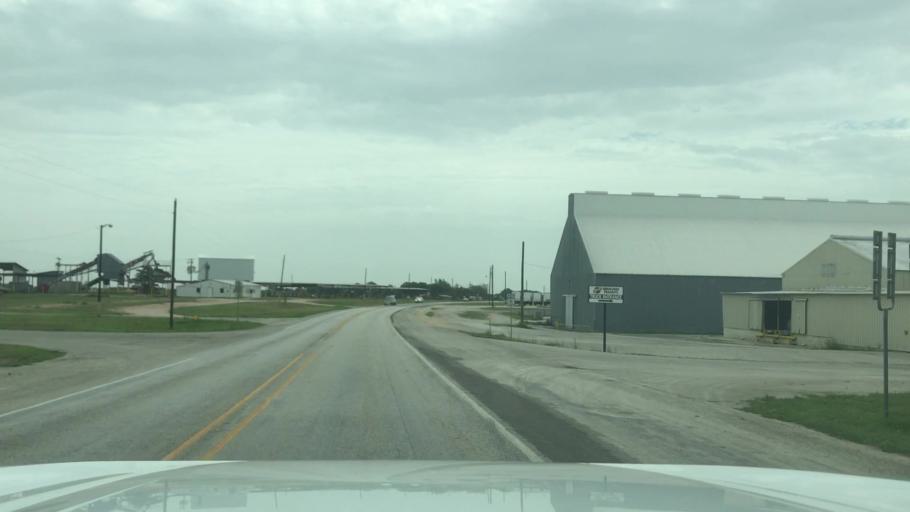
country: US
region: Texas
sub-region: Eastland County
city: Gorman
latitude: 32.2088
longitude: -98.6644
